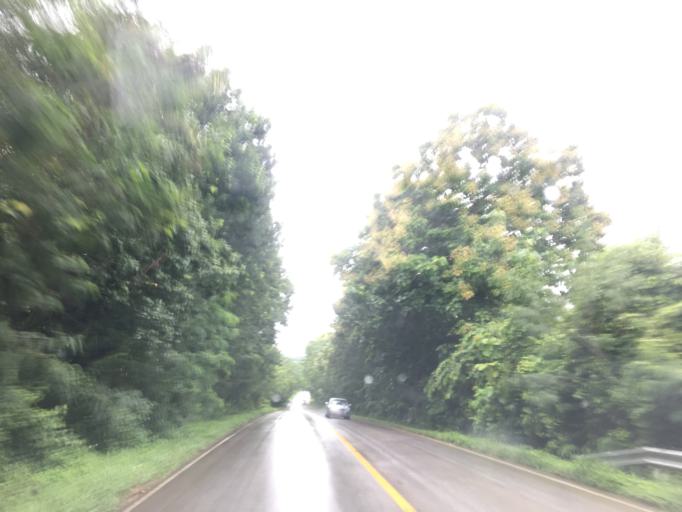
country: TH
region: Chiang Rai
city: Pa Daet
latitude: 19.6227
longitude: 99.9834
